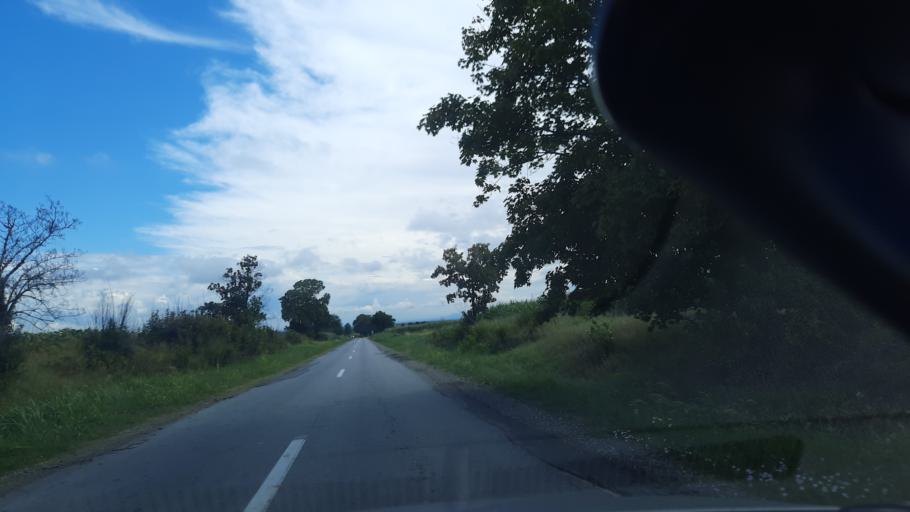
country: RS
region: Autonomna Pokrajina Vojvodina
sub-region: Sremski Okrug
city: Sremska Mitrovica
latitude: 45.1079
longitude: 19.5672
